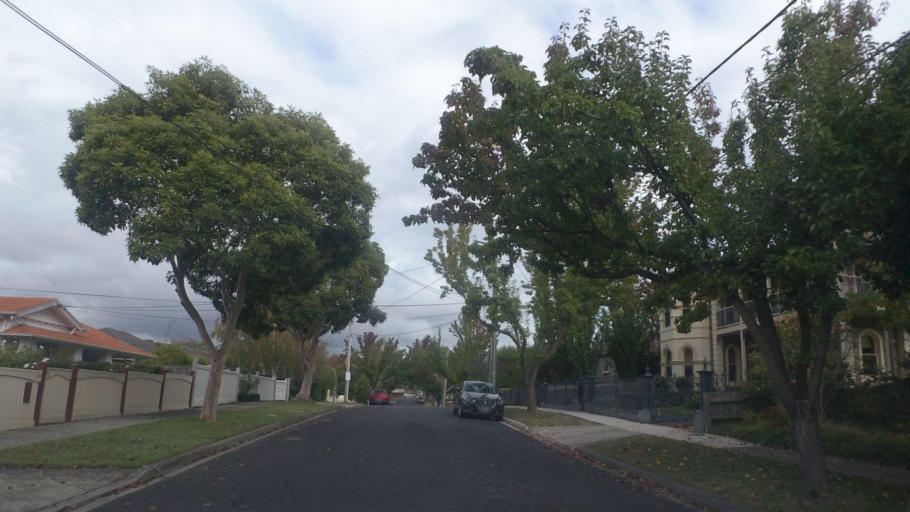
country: AU
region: Victoria
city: Mont Albert
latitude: -37.8202
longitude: 145.1106
